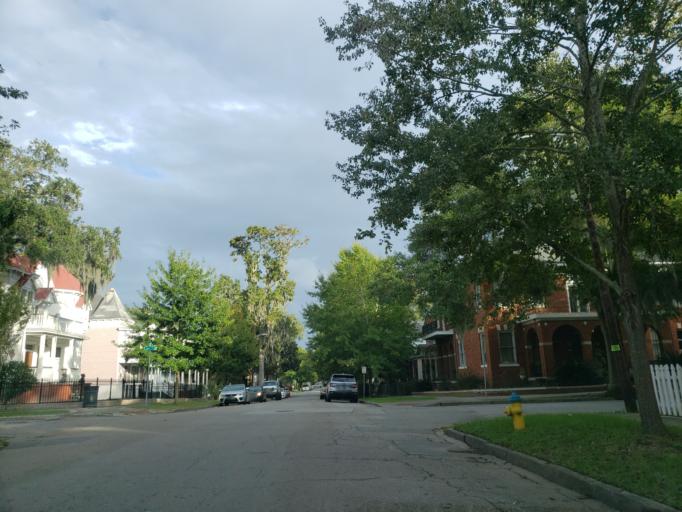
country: US
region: Georgia
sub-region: Chatham County
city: Savannah
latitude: 32.0609
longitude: -81.0823
